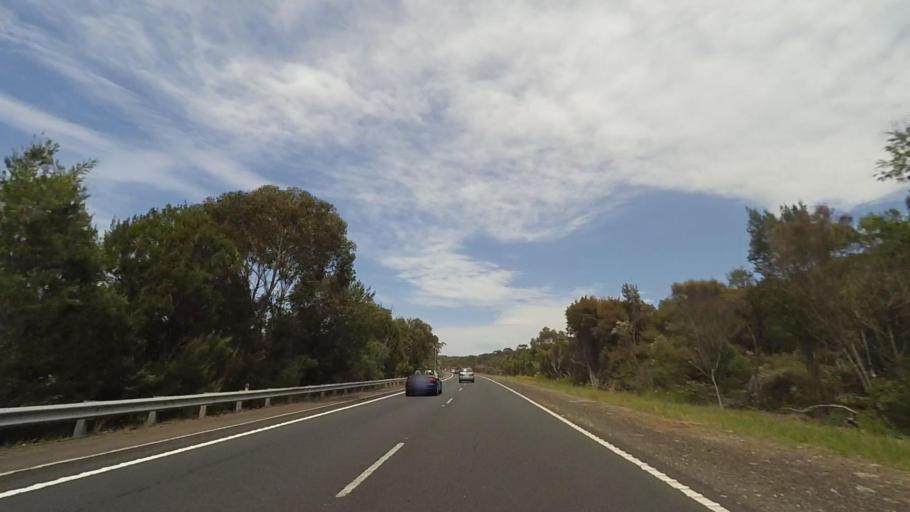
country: AU
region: New South Wales
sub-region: Wollongong
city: Helensburgh
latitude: -34.2283
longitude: 150.9488
